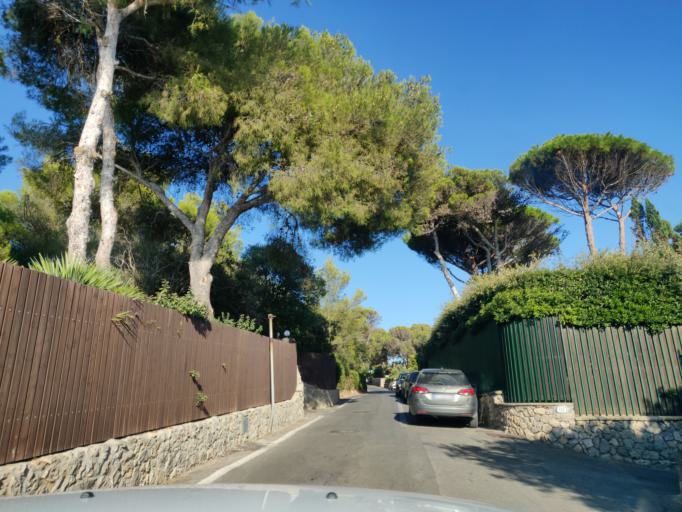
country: IT
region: Tuscany
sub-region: Provincia di Grosseto
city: Orbetello Scalo
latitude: 42.4073
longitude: 11.2854
